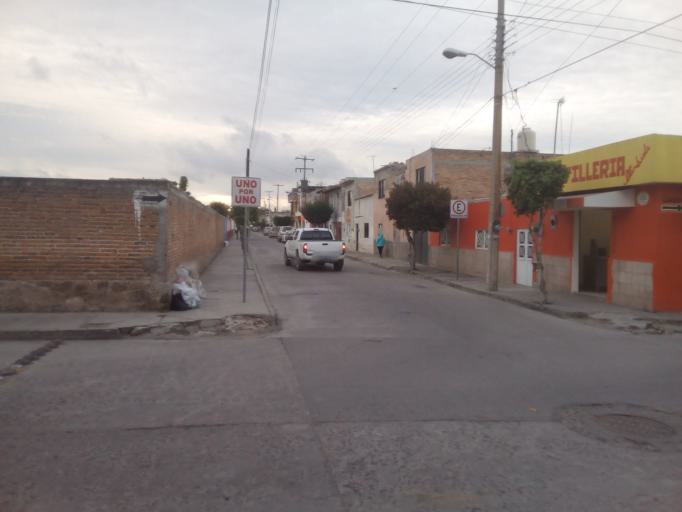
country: MX
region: Guanajuato
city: San Jose Iturbide
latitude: 21.0061
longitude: -100.3858
